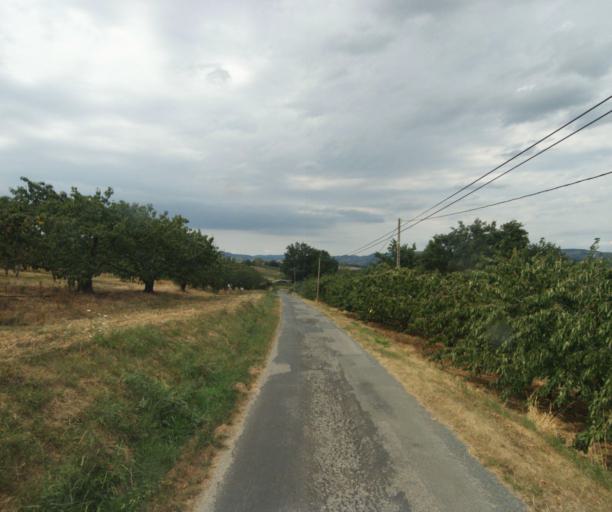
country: FR
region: Rhone-Alpes
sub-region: Departement du Rhone
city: Bully
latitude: 45.8803
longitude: 4.5709
